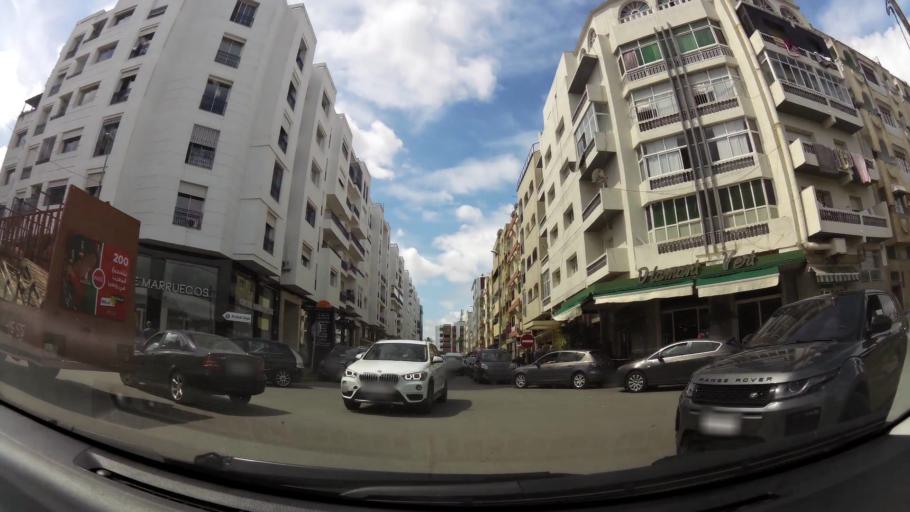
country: MA
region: Grand Casablanca
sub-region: Casablanca
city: Casablanca
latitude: 33.5759
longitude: -7.6492
